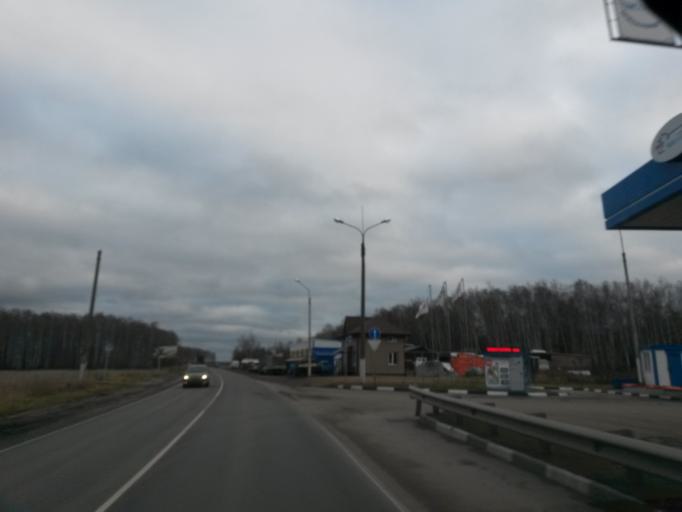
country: RU
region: Moskovskaya
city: Stolbovaya
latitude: 55.2438
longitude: 37.5195
